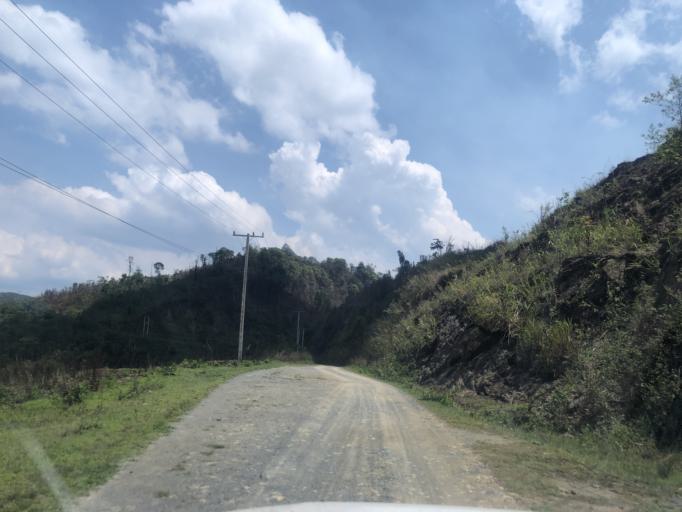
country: LA
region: Phongsali
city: Phongsali
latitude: 21.4007
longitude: 102.1890
